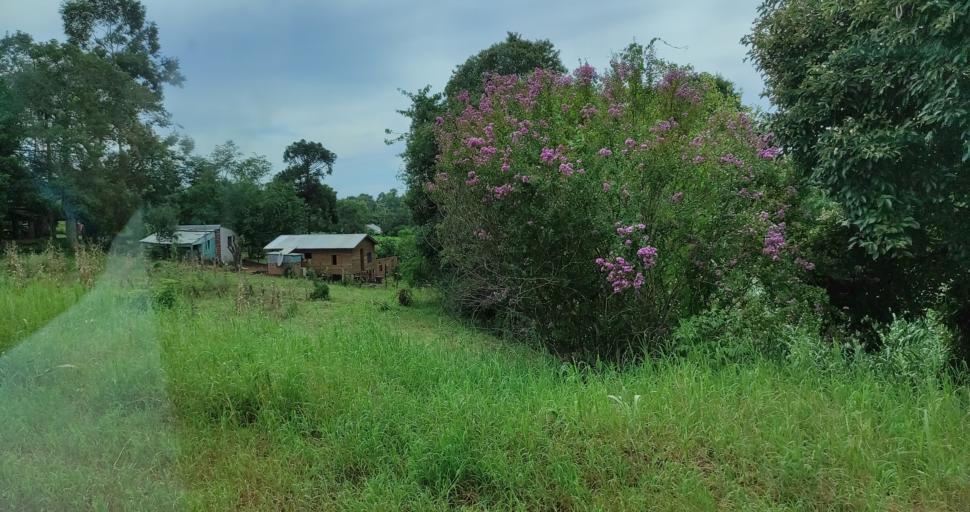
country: AR
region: Misiones
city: El Alcazar
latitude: -26.7205
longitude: -54.8137
